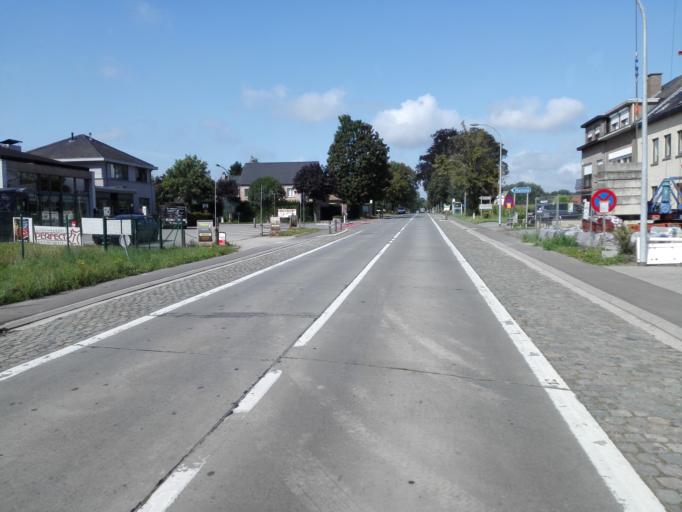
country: BE
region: Flanders
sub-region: Provincie Vlaams-Brabant
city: Wemmel
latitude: 50.9179
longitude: 4.2901
